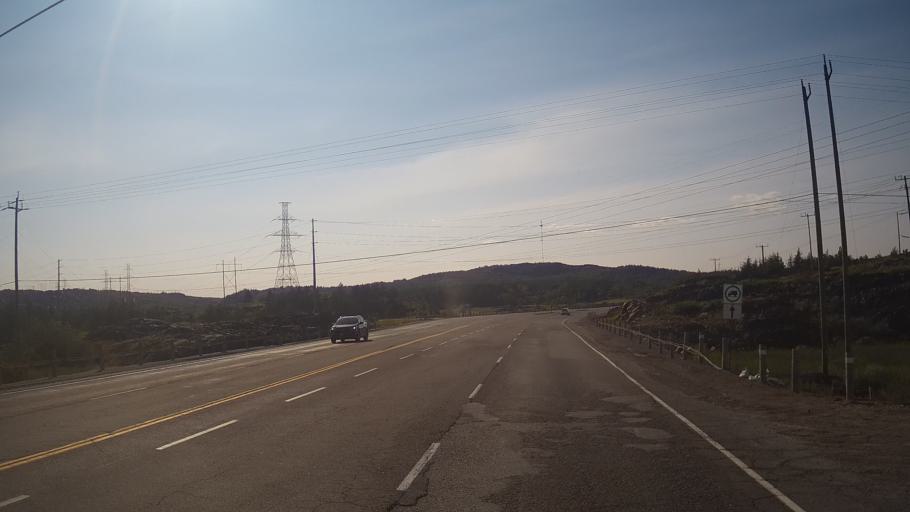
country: CA
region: Ontario
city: Greater Sudbury
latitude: 46.5043
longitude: -81.0441
